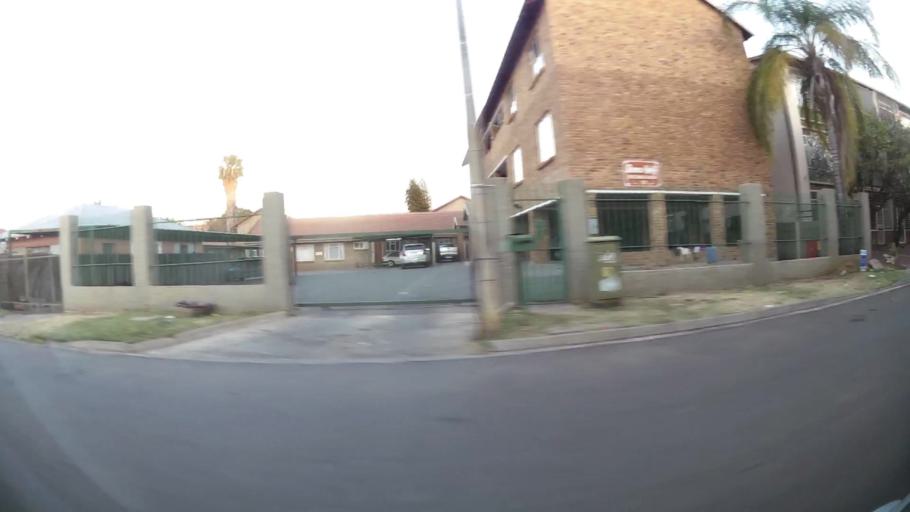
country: ZA
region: North-West
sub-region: Bojanala Platinum District Municipality
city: Rustenburg
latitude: -25.6670
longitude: 27.2475
